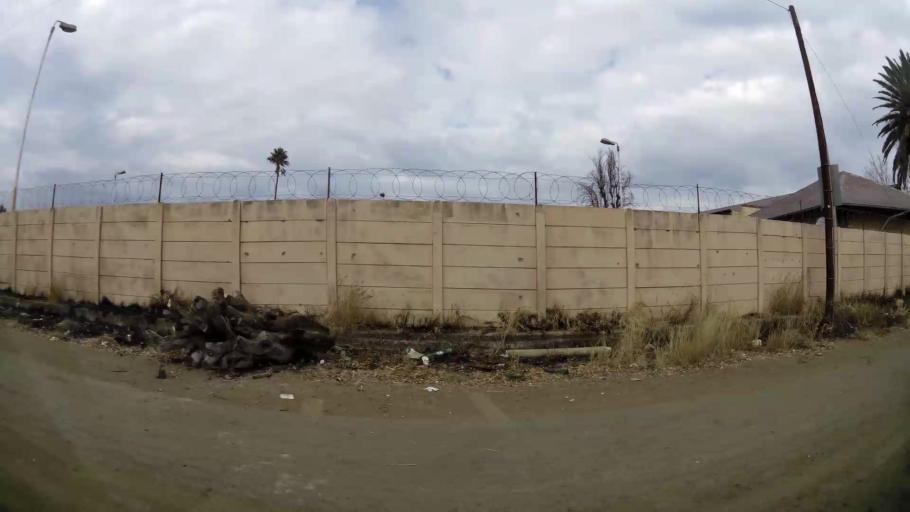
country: ZA
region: Orange Free State
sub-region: Fezile Dabi District Municipality
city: Kroonstad
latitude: -27.6588
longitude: 27.2320
